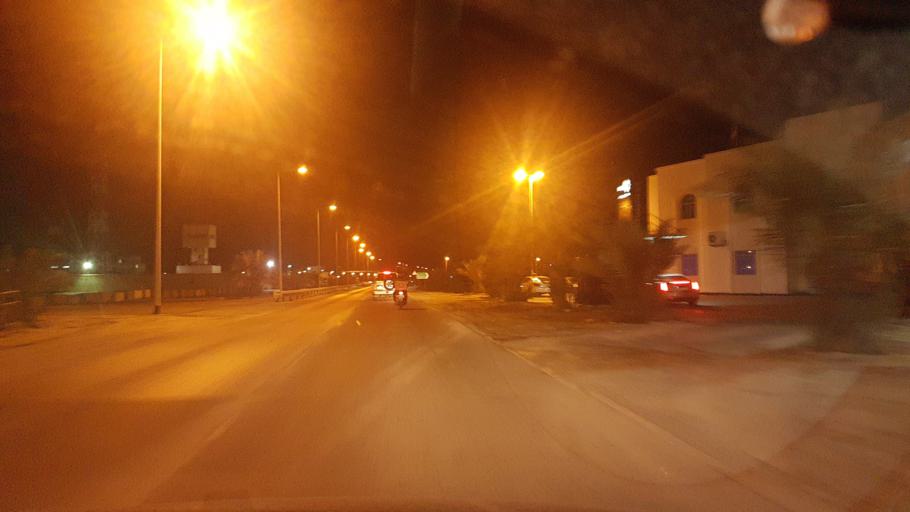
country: BH
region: Muharraq
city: Al Muharraq
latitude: 26.2770
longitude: 50.6358
